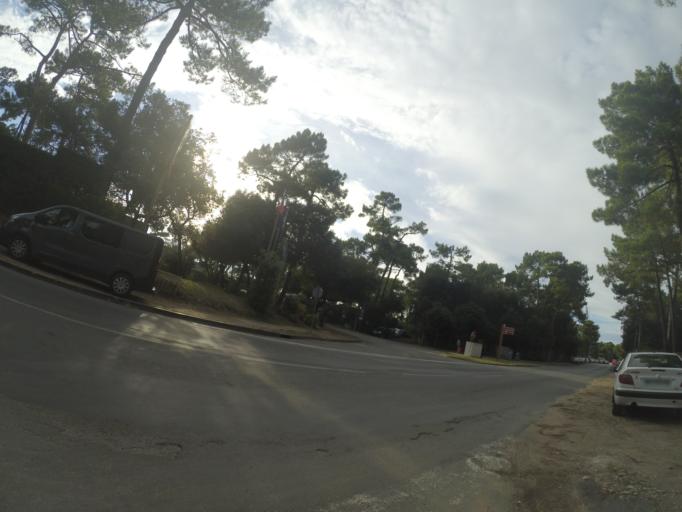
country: FR
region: Poitou-Charentes
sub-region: Departement de la Charente-Maritime
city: Saint-Georges-de-Didonne
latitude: 45.5836
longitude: -0.9852
